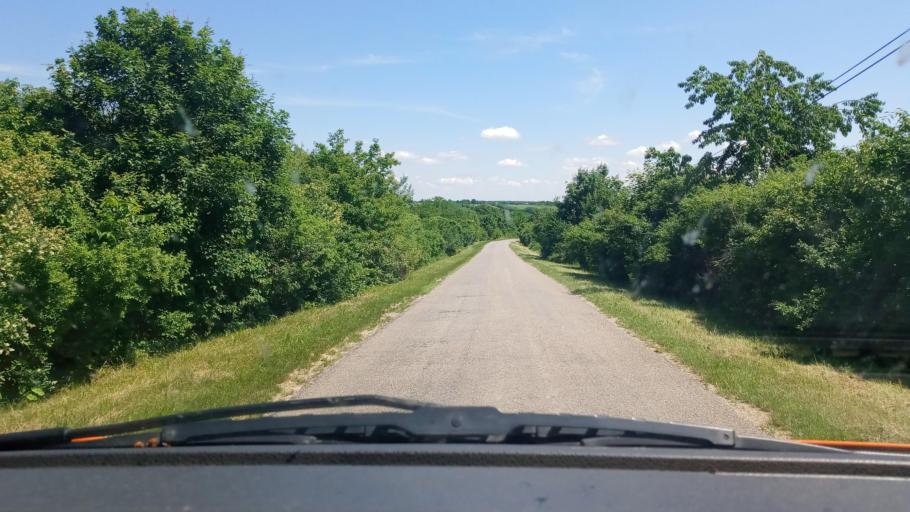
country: HU
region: Baranya
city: Szigetvar
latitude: 46.1742
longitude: 17.7474
